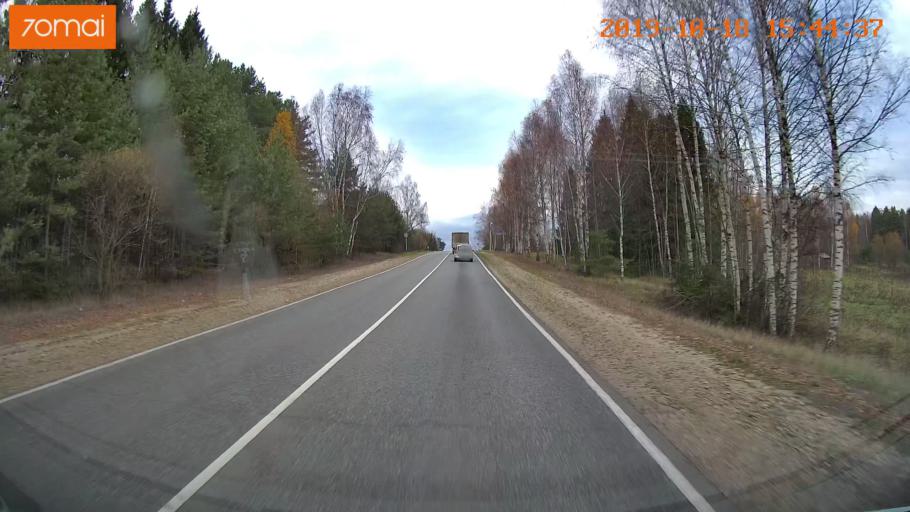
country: RU
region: Vladimir
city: Golovino
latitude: 55.9835
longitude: 40.5528
